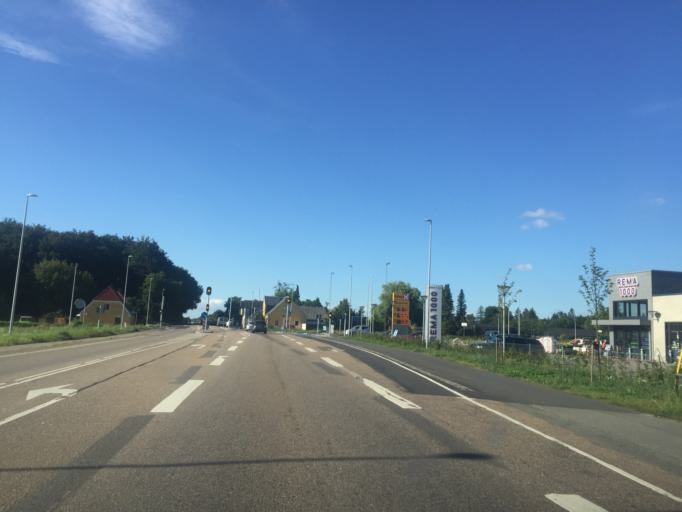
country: DK
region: Zealand
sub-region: Guldborgsund Kommune
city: Nykobing Falster
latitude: 54.8072
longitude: 11.8715
